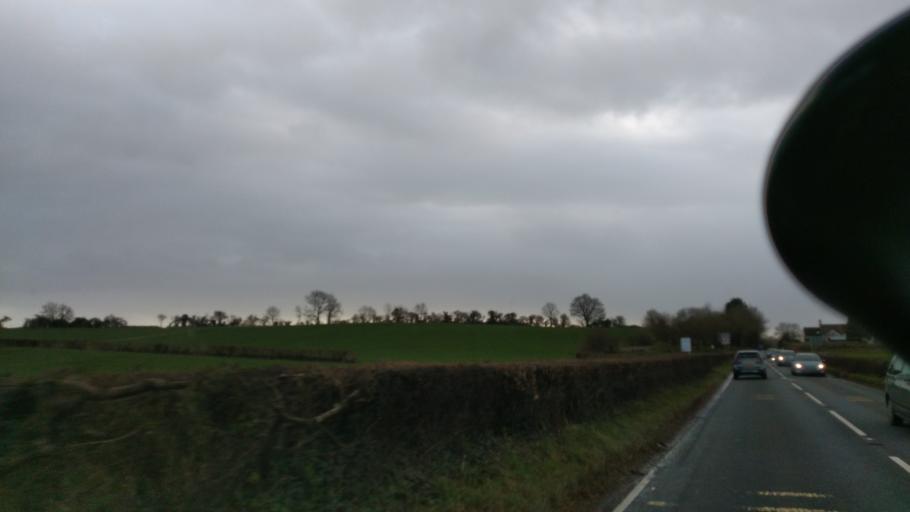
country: GB
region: England
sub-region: Somerset
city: Shepton Mallet
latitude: 51.1680
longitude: -2.5380
